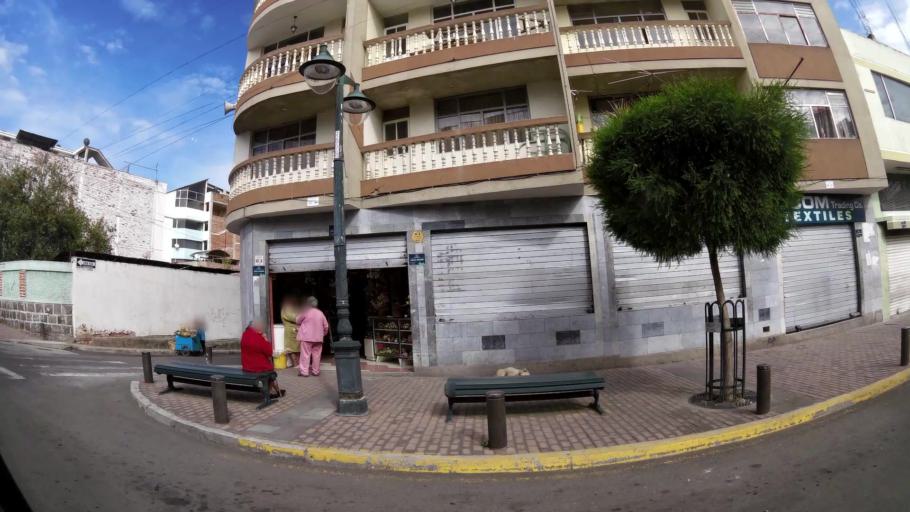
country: EC
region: Tungurahua
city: Ambato
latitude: -1.2456
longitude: -78.6371
